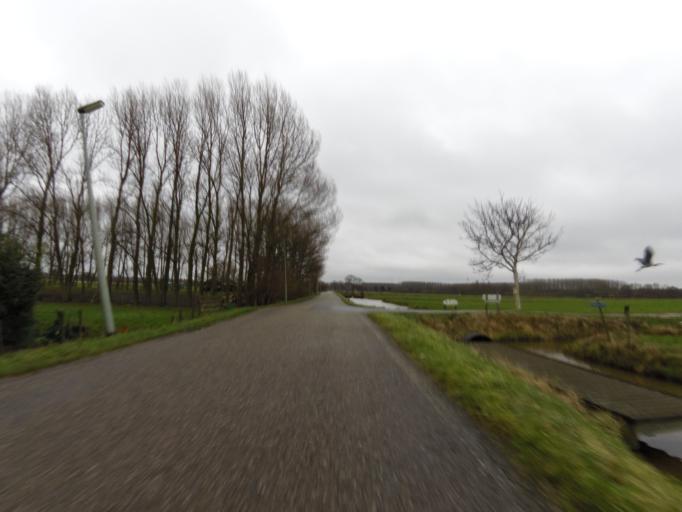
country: NL
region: South Holland
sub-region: Gemeente Maassluis
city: Maassluis
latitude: 51.9155
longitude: 4.2897
